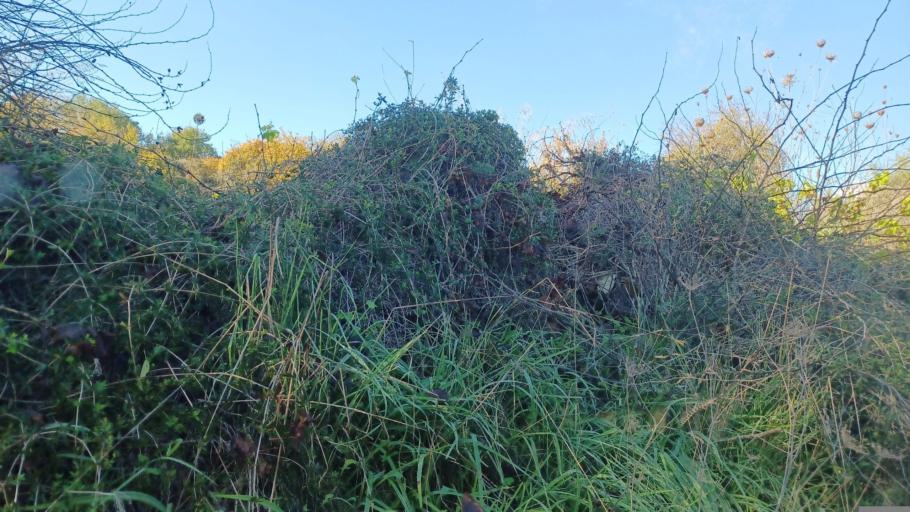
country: CY
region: Pafos
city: Mesogi
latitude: 34.8438
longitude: 32.5301
